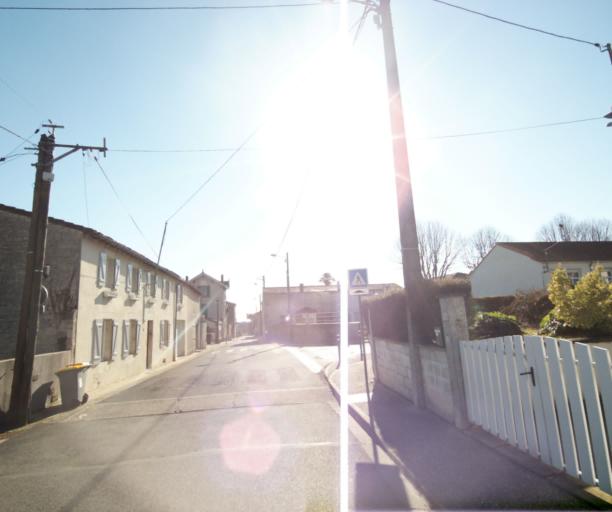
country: FR
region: Poitou-Charentes
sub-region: Departement des Deux-Sevres
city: Niort
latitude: 46.3470
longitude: -0.4716
